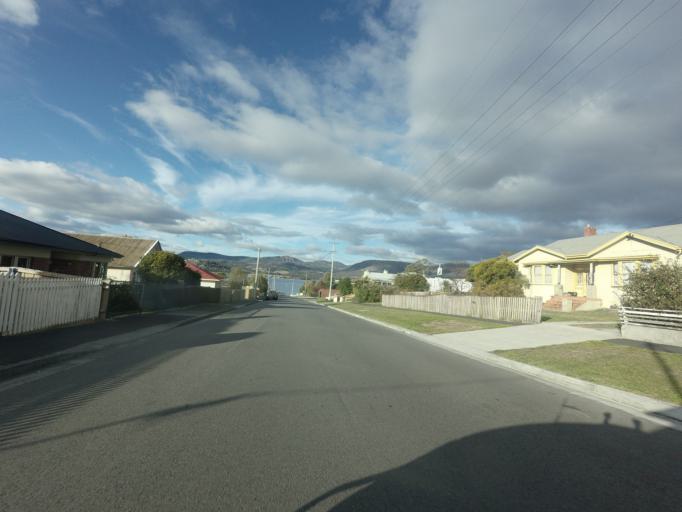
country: AU
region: Tasmania
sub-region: Glenorchy
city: Claremont
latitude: -42.7865
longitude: 147.2493
